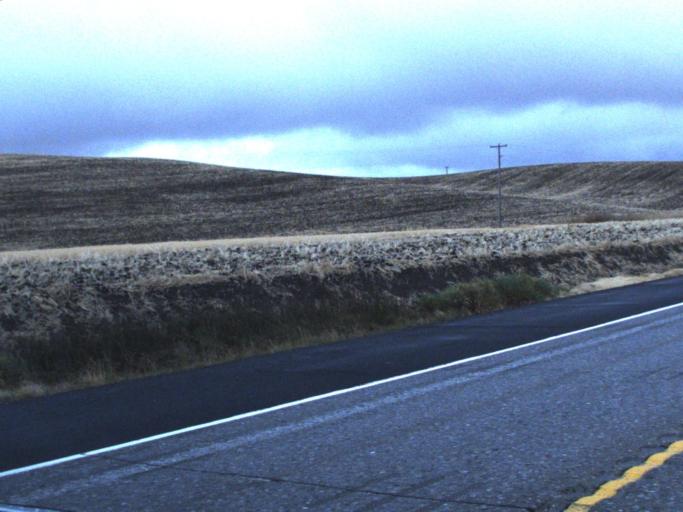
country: US
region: Washington
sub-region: Whitman County
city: Colfax
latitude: 47.0526
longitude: -117.3805
